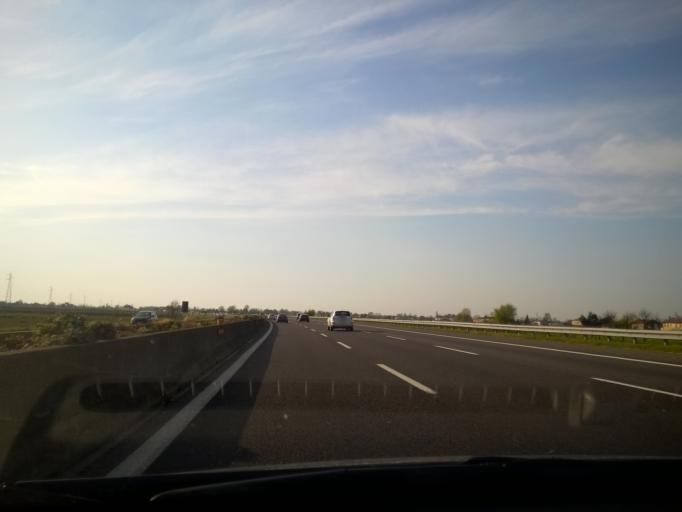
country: IT
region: Emilia-Romagna
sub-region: Forli-Cesena
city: Forli
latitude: 44.2790
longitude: 12.0231
